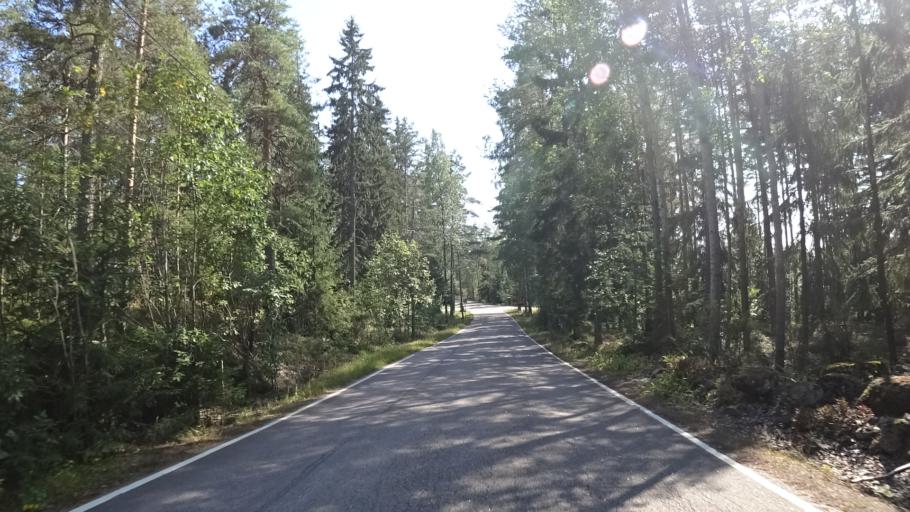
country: FI
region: Kymenlaakso
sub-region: Kotka-Hamina
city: Karhula
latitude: 60.5587
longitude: 26.9003
